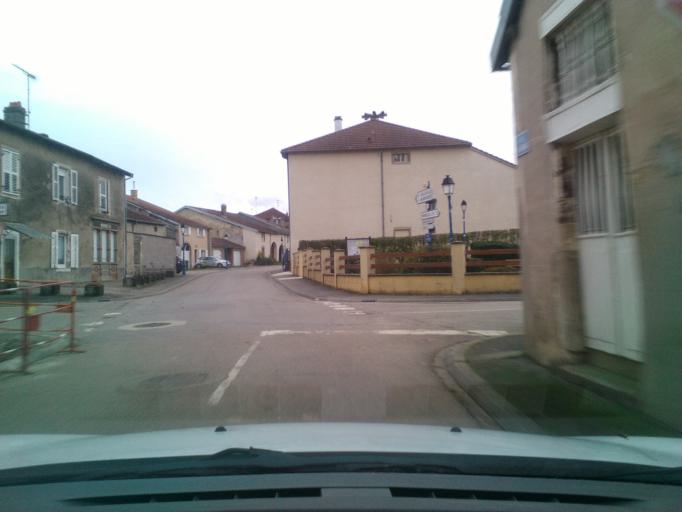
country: FR
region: Lorraine
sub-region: Departement des Vosges
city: Mirecourt
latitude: 48.3316
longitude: 6.0583
